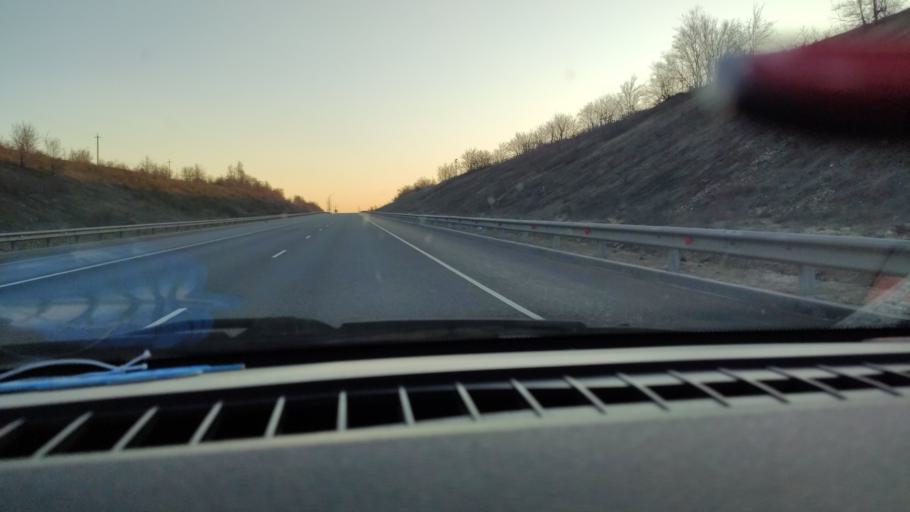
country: RU
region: Saratov
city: Yelshanka
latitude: 51.8884
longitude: 46.5201
